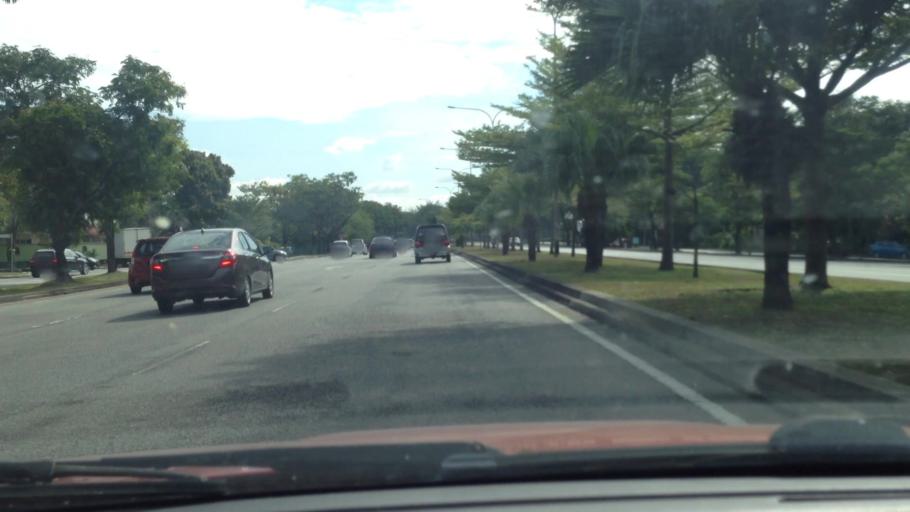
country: MY
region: Selangor
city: Subang Jaya
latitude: 3.0584
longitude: 101.5788
